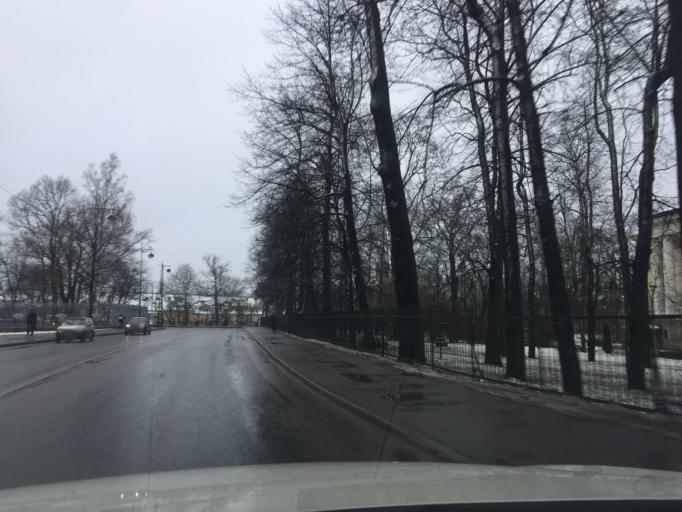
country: RU
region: St.-Petersburg
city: Pushkin
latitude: 59.7124
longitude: 30.4104
